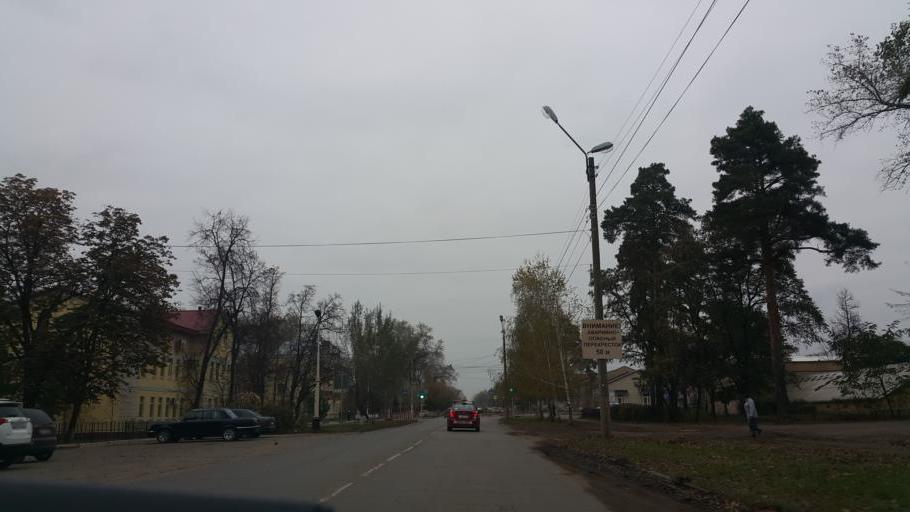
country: RU
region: Tambov
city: Kotovsk
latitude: 52.5865
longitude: 41.5025
